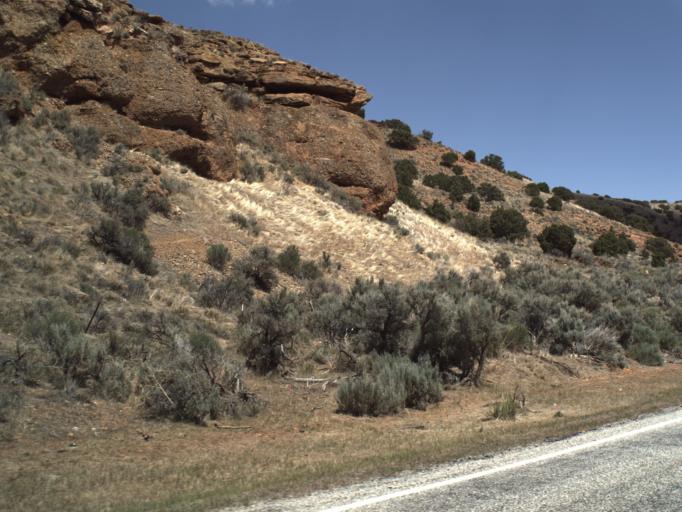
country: US
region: Utah
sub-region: Rich County
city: Randolph
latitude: 41.5009
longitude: -111.2792
